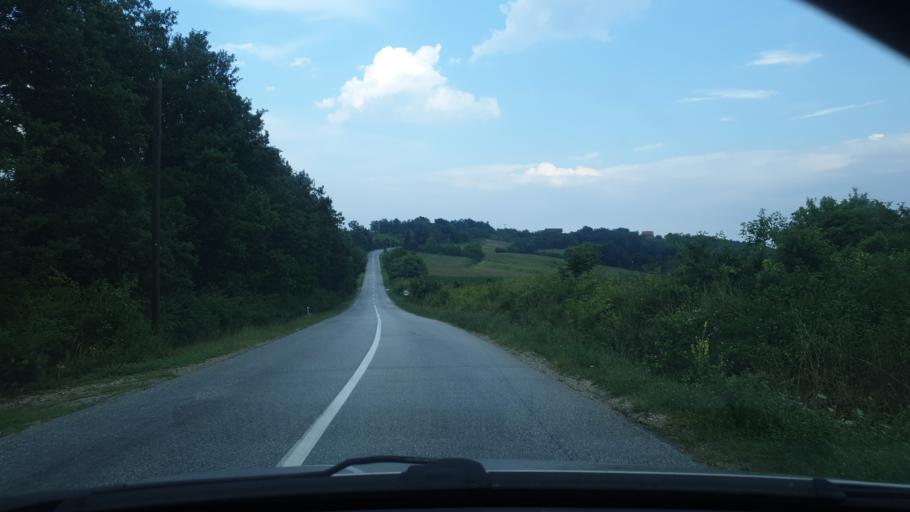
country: RS
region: Central Serbia
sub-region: Sumadijski Okrug
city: Kragujevac
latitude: 44.0455
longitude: 20.7881
